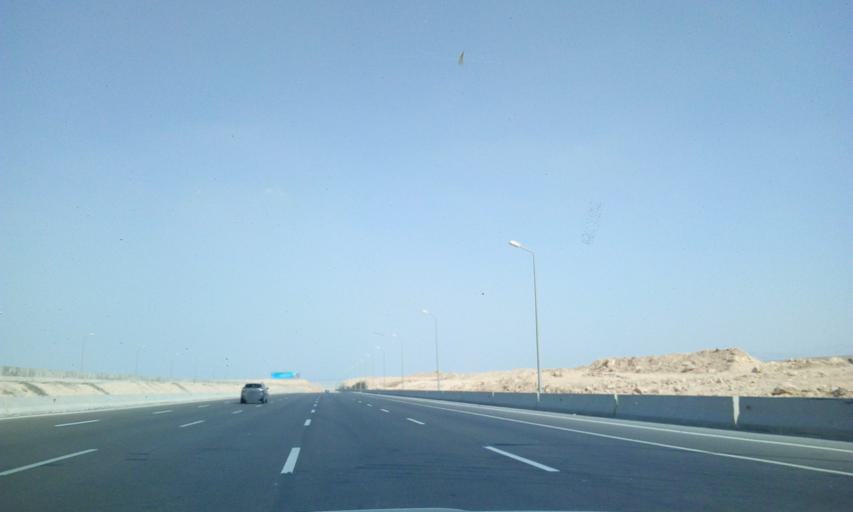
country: EG
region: As Suways
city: Ain Sukhna
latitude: 29.6857
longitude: 32.1993
